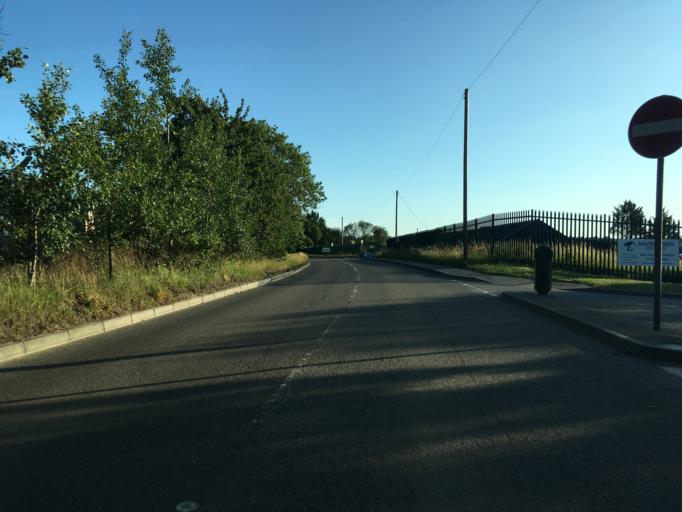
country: GB
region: England
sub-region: Hampshire
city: Tadley
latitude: 51.3674
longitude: -1.1534
